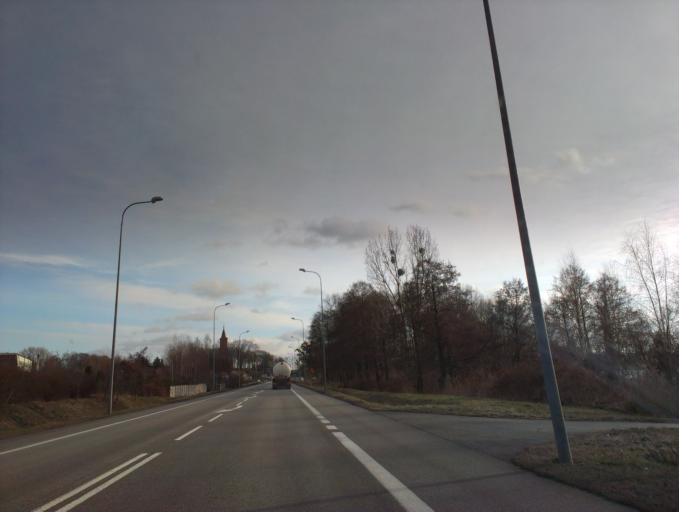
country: PL
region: Kujawsko-Pomorskie
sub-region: Powiat lipnowski
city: Kikol
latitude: 52.9126
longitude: 19.1150
